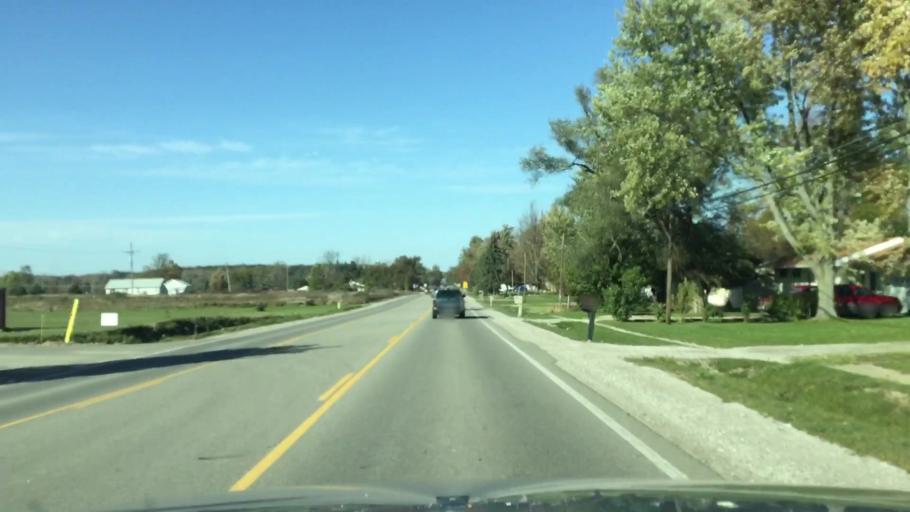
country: US
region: Michigan
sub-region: Lapeer County
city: Lapeer
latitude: 43.0613
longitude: -83.3431
